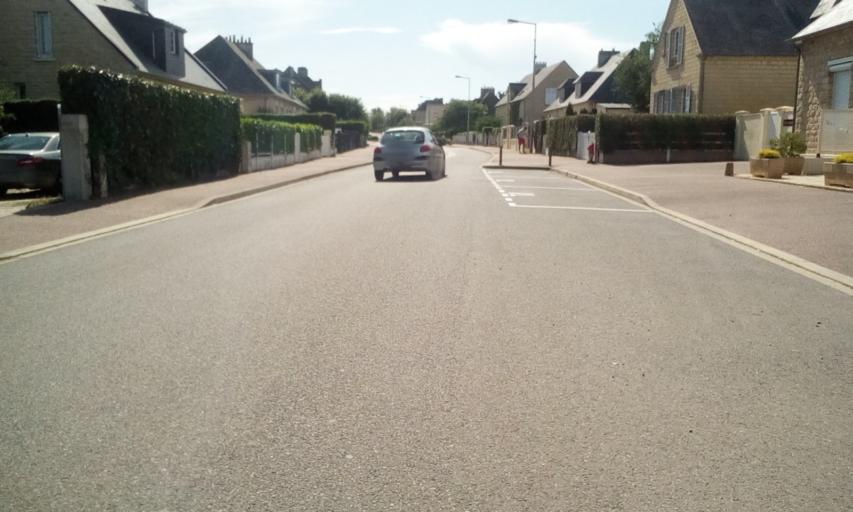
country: FR
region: Lower Normandy
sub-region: Departement du Calvados
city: Eterville
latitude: 49.1303
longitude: -0.4206
